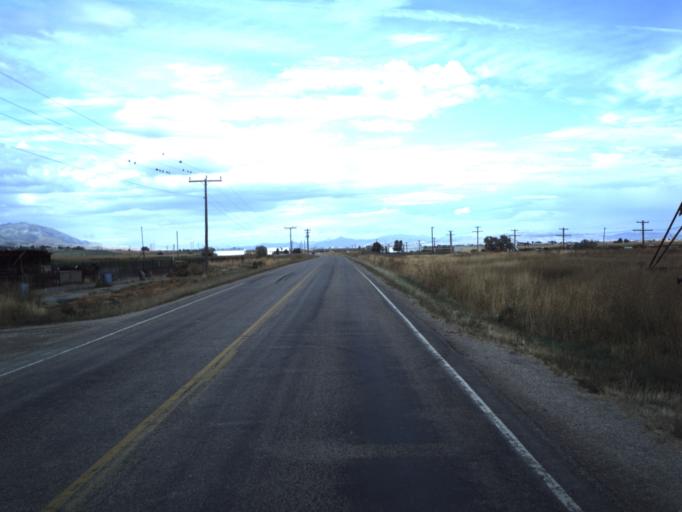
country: US
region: Utah
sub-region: Cache County
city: Lewiston
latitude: 41.9989
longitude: -111.9550
